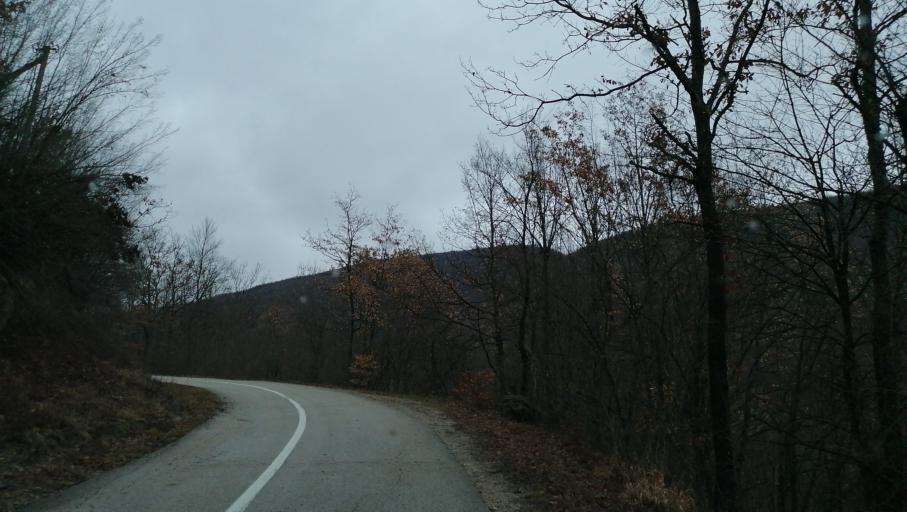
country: RS
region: Central Serbia
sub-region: Pirotski Okrug
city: Dimitrovgrad
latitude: 42.9819
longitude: 22.7836
